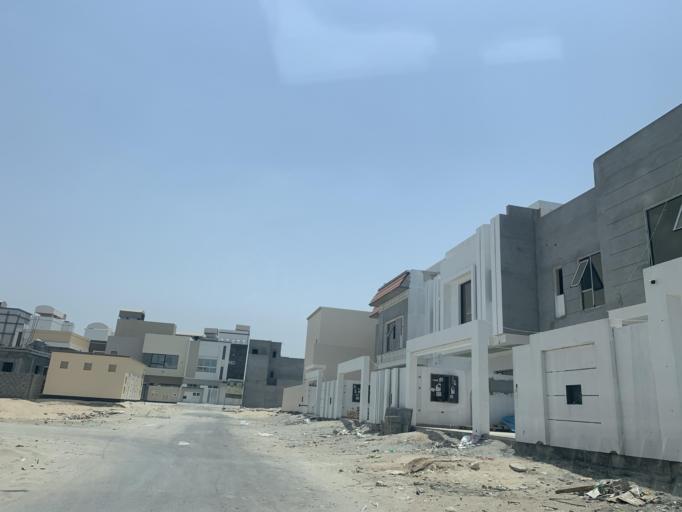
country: BH
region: Manama
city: Jidd Hafs
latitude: 26.2120
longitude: 50.4691
